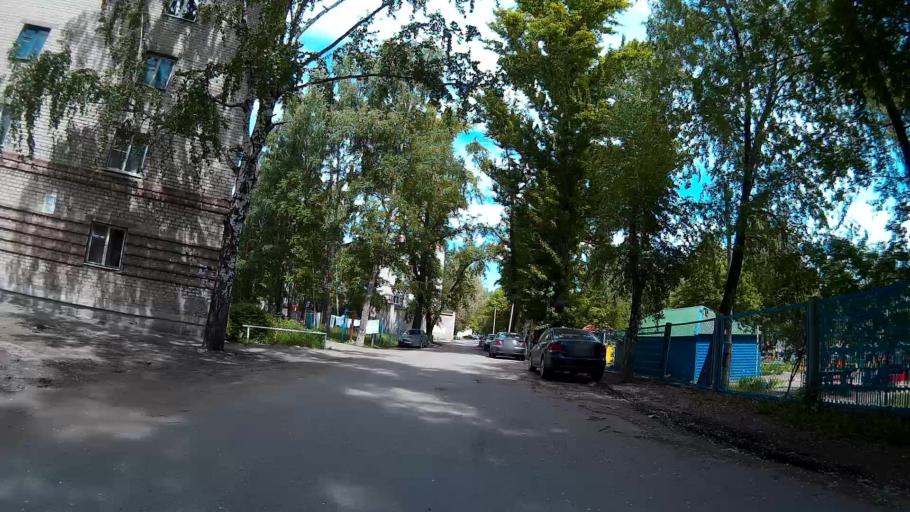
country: RU
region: Ulyanovsk
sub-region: Ulyanovskiy Rayon
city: Ulyanovsk
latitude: 54.2876
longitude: 48.3662
